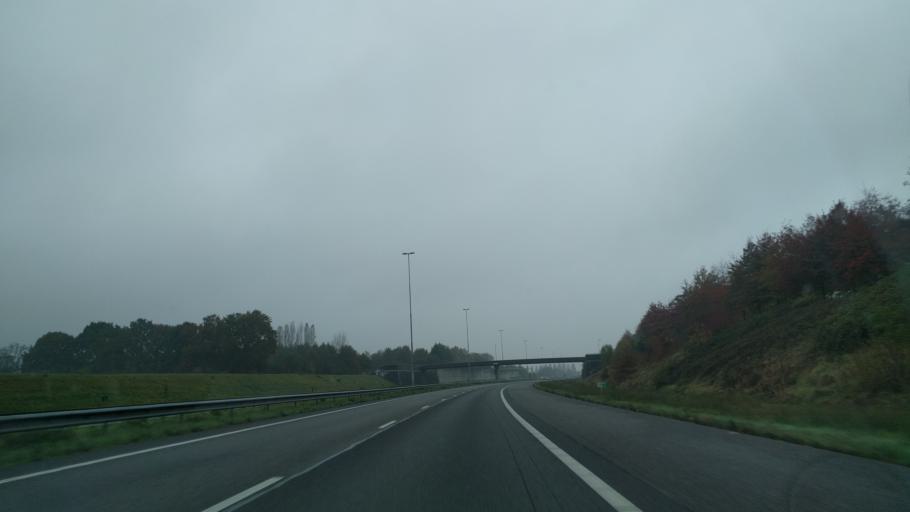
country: NL
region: North Brabant
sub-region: Gemeente Zundert
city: Zundert
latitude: 51.5573
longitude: 4.6500
